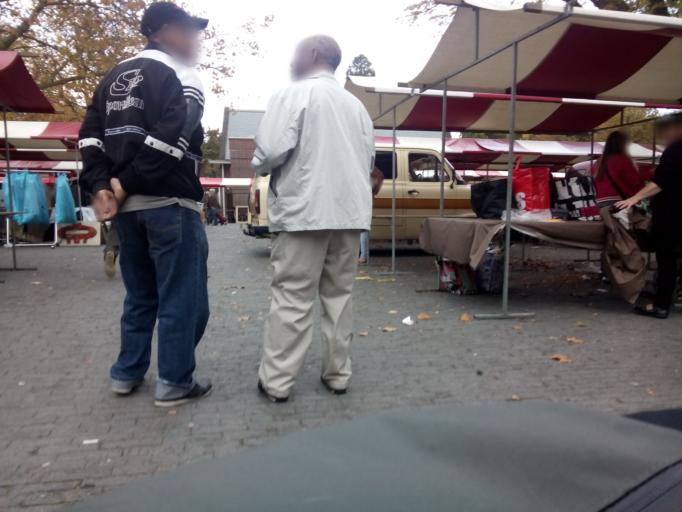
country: NL
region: South Holland
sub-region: Gemeente Rotterdam
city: Delfshaven
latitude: 51.9129
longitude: 4.4544
